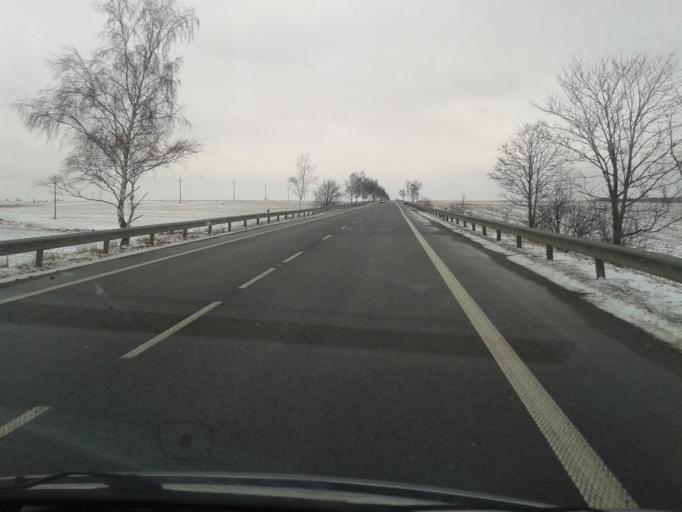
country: SK
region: Zilinsky
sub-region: Okres Zilina
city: Trstena
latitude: 49.3818
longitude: 19.6334
